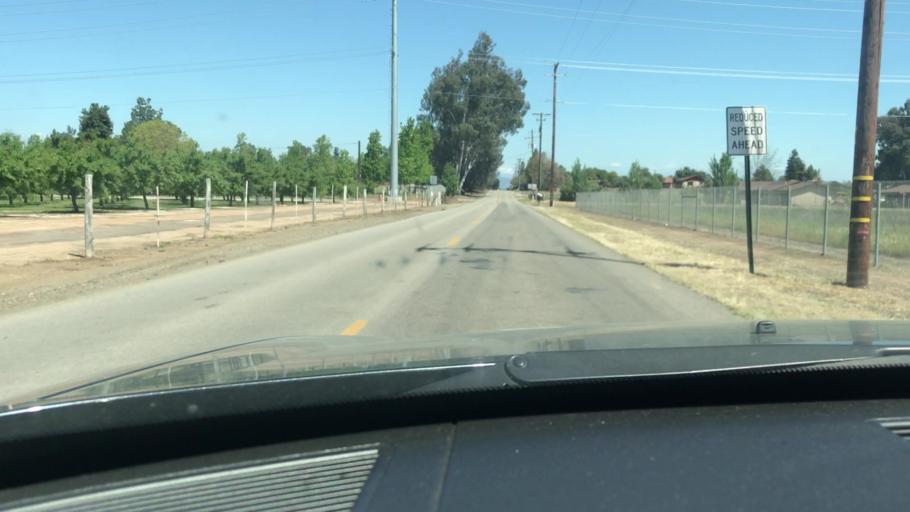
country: US
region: California
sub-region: Fresno County
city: Clovis
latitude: 36.8810
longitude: -119.6942
